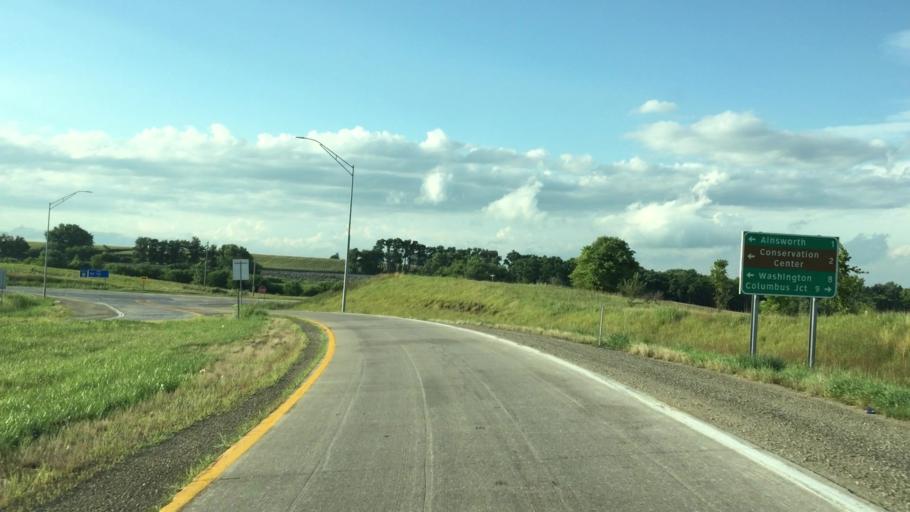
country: US
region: Iowa
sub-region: Washington County
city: Washington
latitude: 41.2903
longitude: -91.5314
